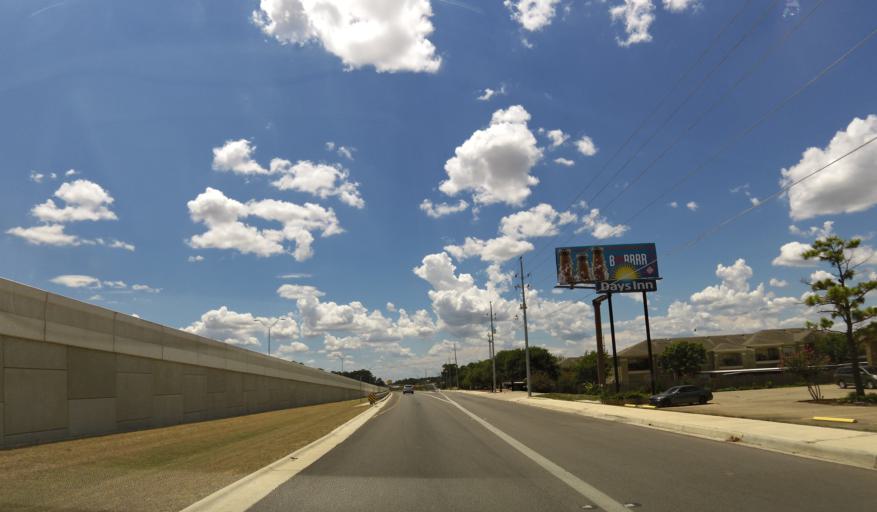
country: US
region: Texas
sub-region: Bastrop County
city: Bastrop
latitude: 30.1031
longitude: -97.2860
